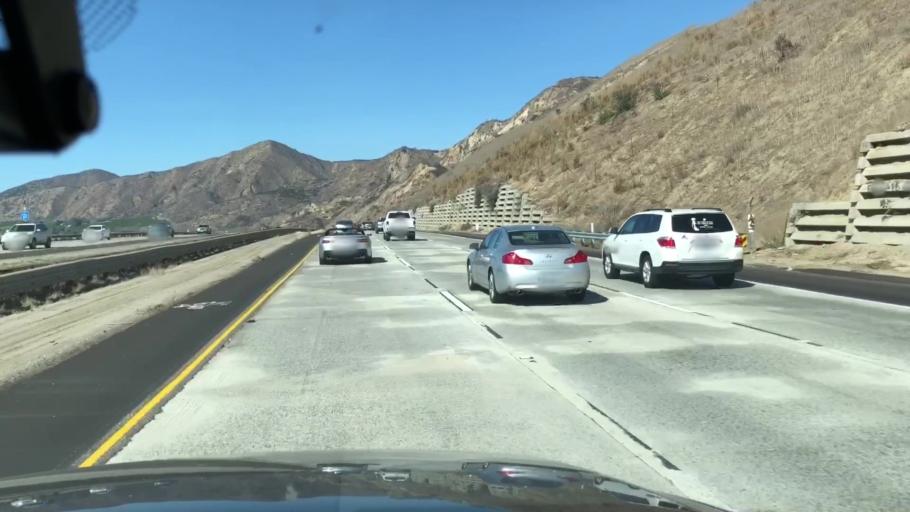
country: US
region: California
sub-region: Ventura County
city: Ventura
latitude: 34.3144
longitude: -119.3597
